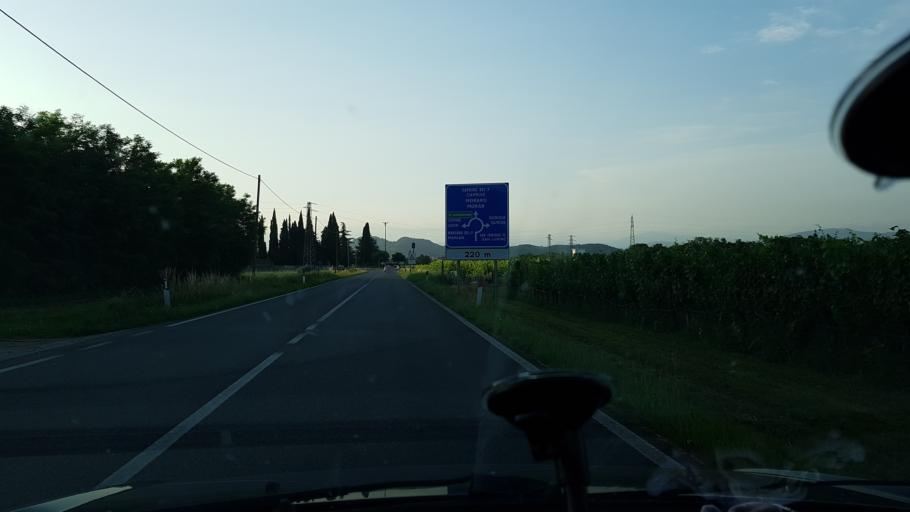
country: IT
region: Friuli Venezia Giulia
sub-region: Provincia di Gorizia
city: Moraro
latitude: 45.9216
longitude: 13.4988
